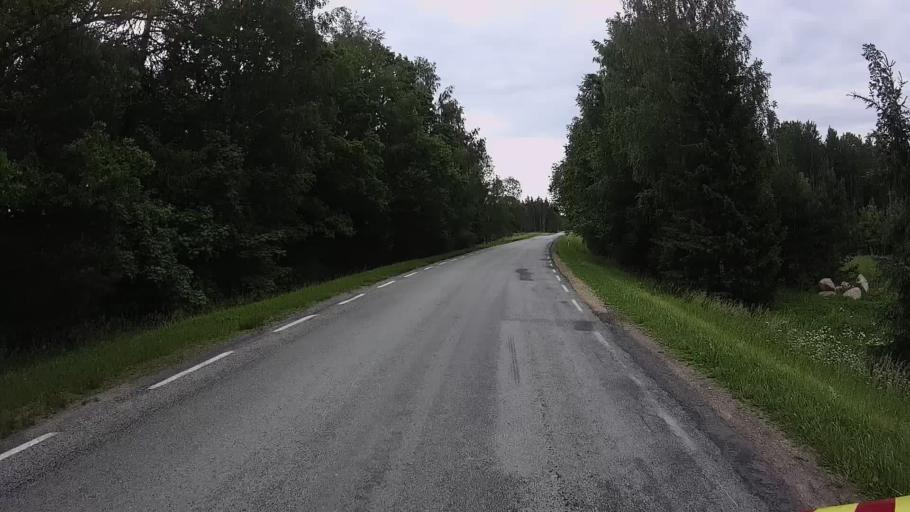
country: EE
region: Viljandimaa
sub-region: Karksi vald
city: Karksi-Nuia
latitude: 58.2239
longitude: 25.6138
